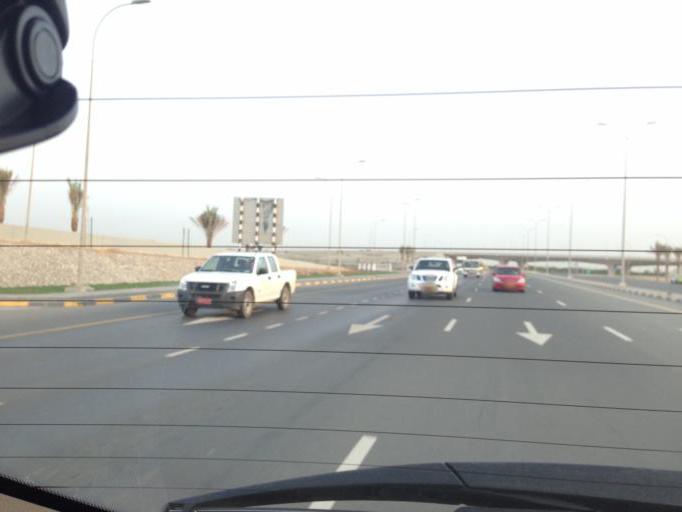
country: OM
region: Muhafazat Masqat
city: Bawshar
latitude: 23.6052
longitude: 58.3111
